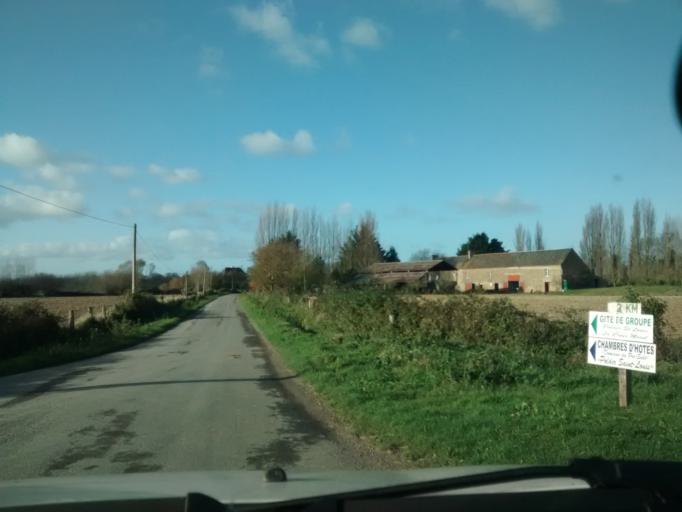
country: FR
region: Brittany
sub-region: Departement d'Ille-et-Vilaine
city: Roz-sur-Couesnon
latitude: 48.6059
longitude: -1.6040
